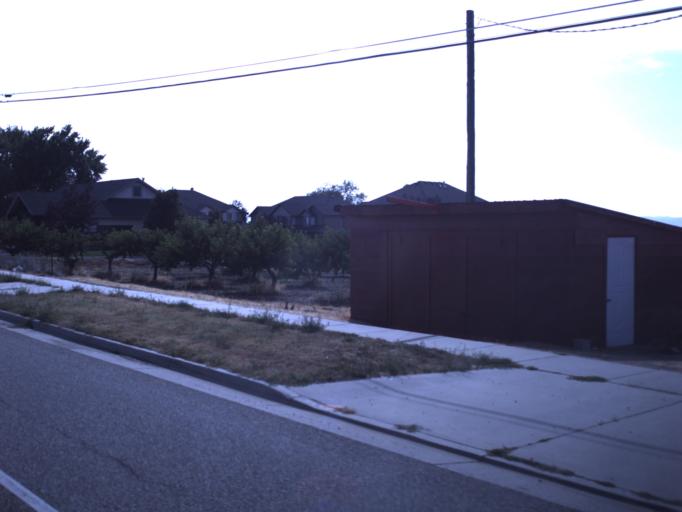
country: US
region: Utah
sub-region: Box Elder County
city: Perry
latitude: 41.4677
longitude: -112.0314
